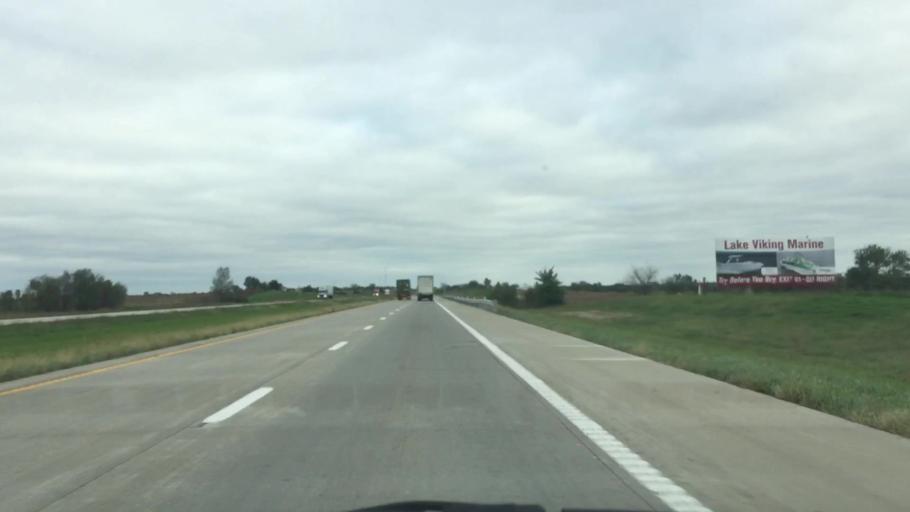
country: US
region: Missouri
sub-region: Clinton County
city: Lathrop
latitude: 39.5773
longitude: -94.2601
